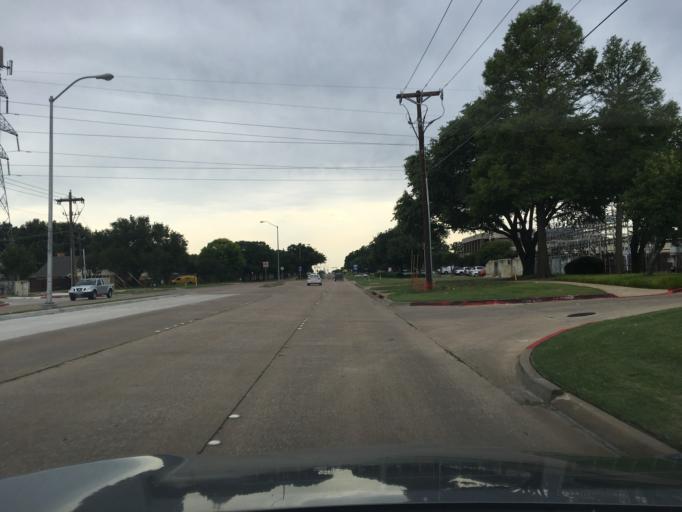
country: US
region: Texas
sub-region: Dallas County
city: Richardson
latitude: 32.9574
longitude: -96.7000
